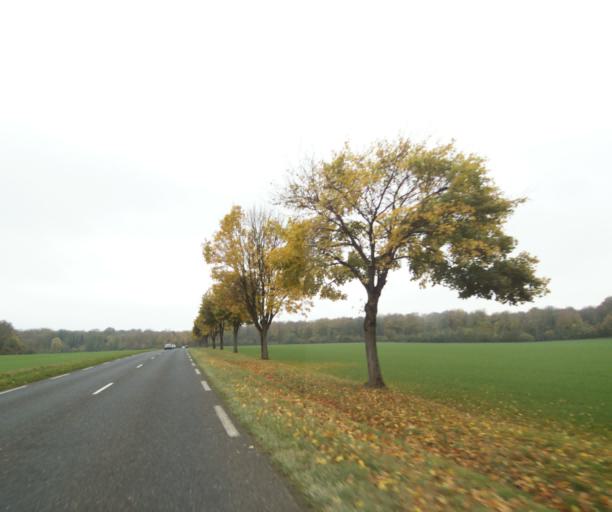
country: FR
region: Lorraine
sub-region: Departement de Meurthe-et-Moselle
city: Briey
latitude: 49.2779
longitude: 5.9594
